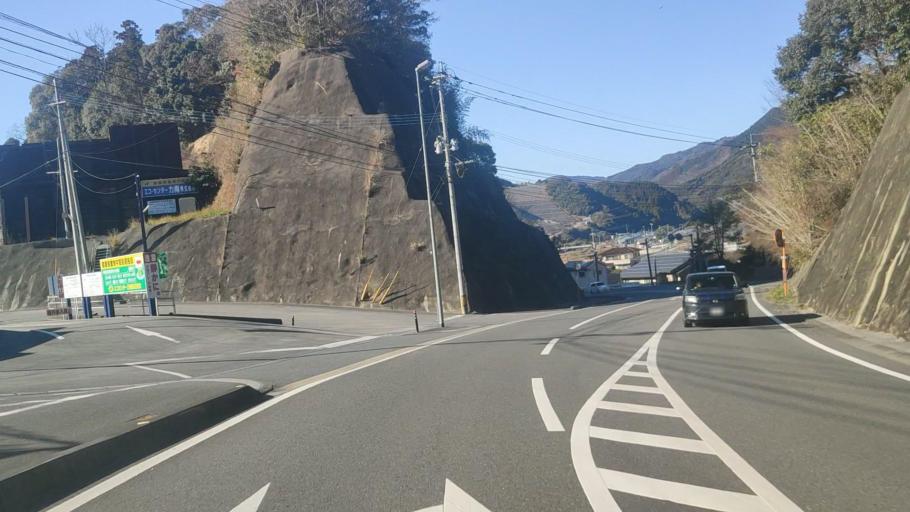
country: JP
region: Oita
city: Saiki
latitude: 32.9762
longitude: 131.8537
